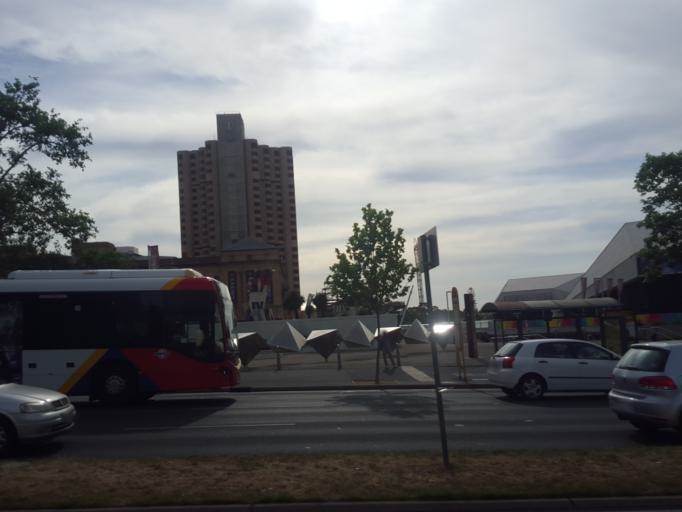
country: AU
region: South Australia
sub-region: Adelaide
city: Adelaide
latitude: -34.9202
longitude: 138.5993
